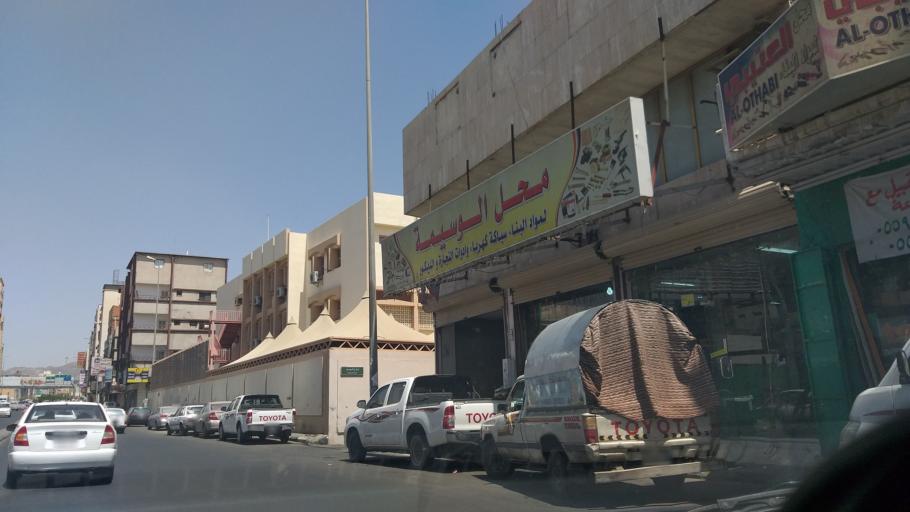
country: SA
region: Makkah
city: Ta'if
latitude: 21.2683
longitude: 40.4145
